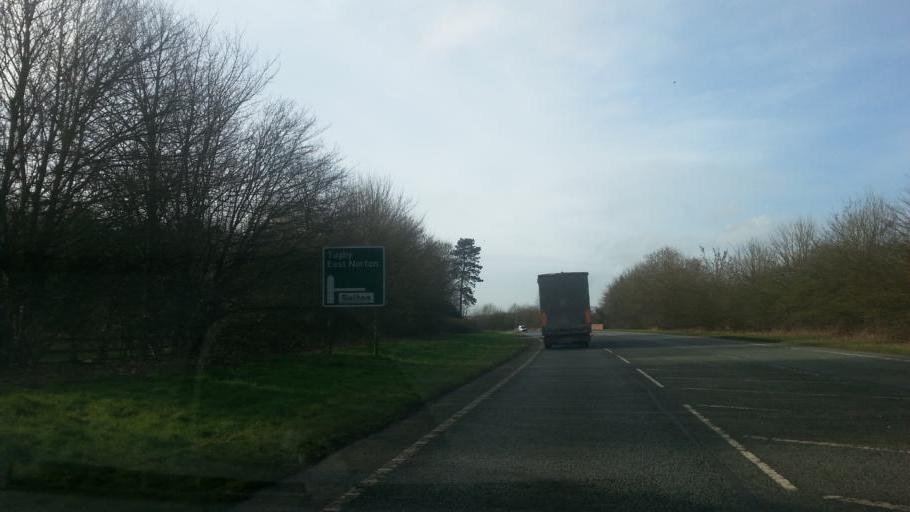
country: GB
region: England
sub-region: District of Rutland
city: Ridlington
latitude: 52.5979
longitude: -0.7964
